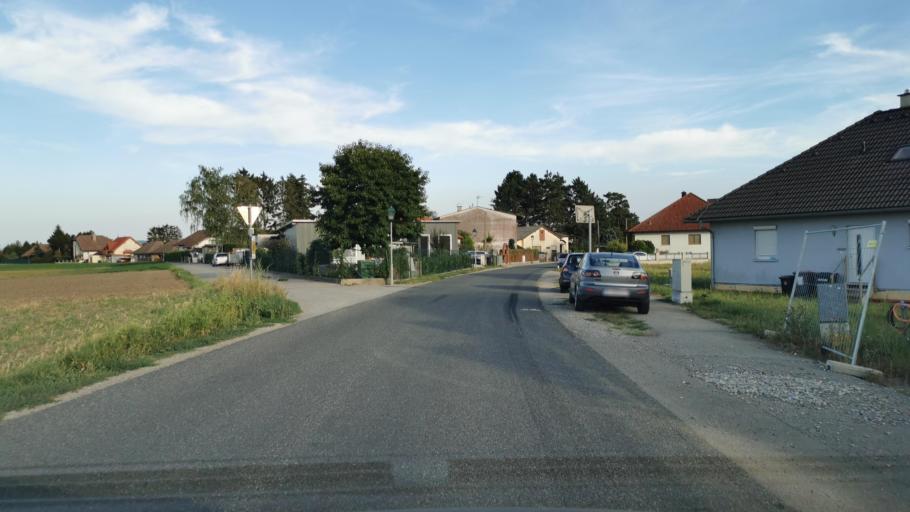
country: AT
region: Lower Austria
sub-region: Politischer Bezirk Tulln
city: Michelhausen
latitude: 48.3246
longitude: 15.9587
